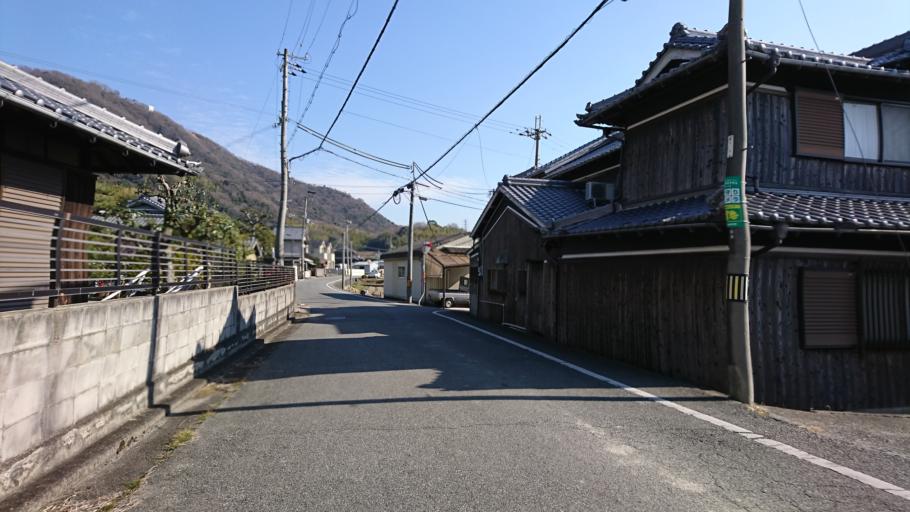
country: JP
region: Hyogo
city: Kakogawacho-honmachi
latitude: 34.8304
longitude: 134.8444
